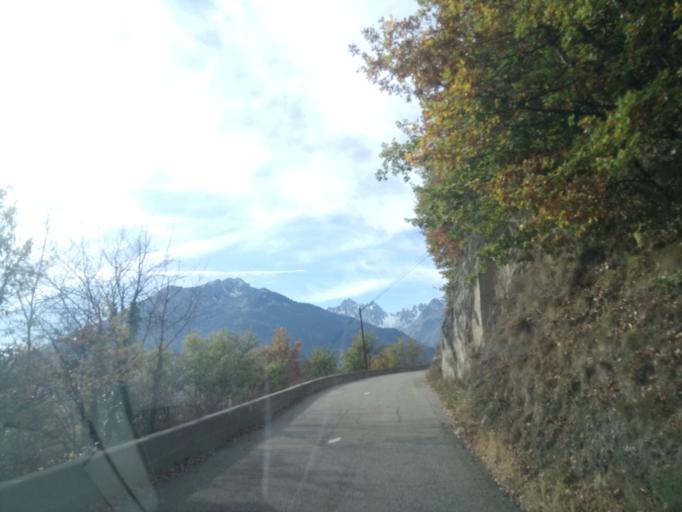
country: FR
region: Rhone-Alpes
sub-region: Departement de la Savoie
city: La Chambre
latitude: 45.3724
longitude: 6.3052
